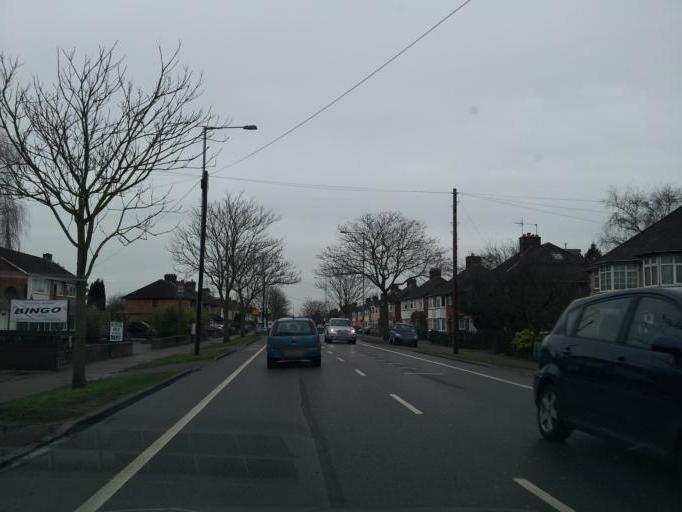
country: GB
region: England
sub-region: Cambridgeshire
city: Cambridge
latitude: 52.1888
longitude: 0.1533
